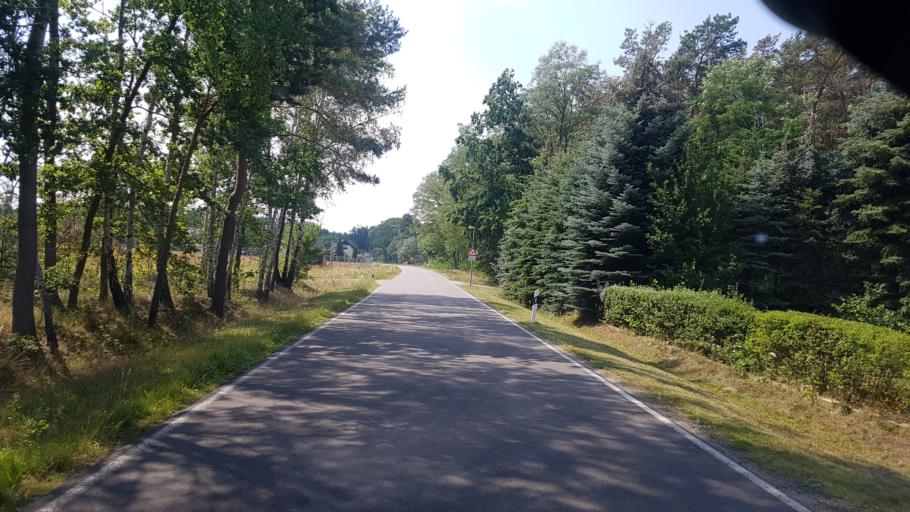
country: DE
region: Brandenburg
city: Cottbus
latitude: 51.6894
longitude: 14.4175
